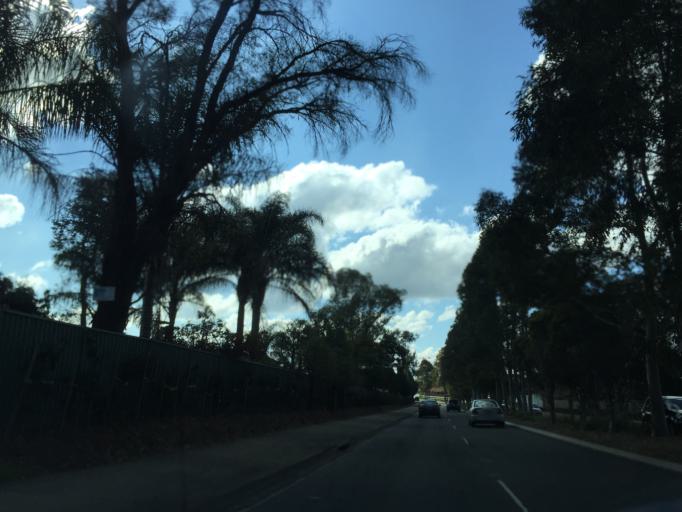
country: AU
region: New South Wales
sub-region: Blacktown
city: Quakers Hill
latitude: -33.7228
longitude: 150.8905
